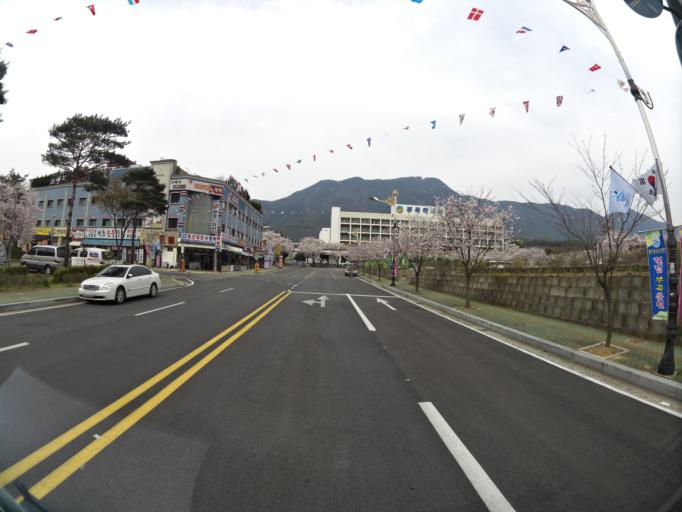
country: KR
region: Gyeongsangnam-do
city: Changnyeong
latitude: 35.4375
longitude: 128.5913
